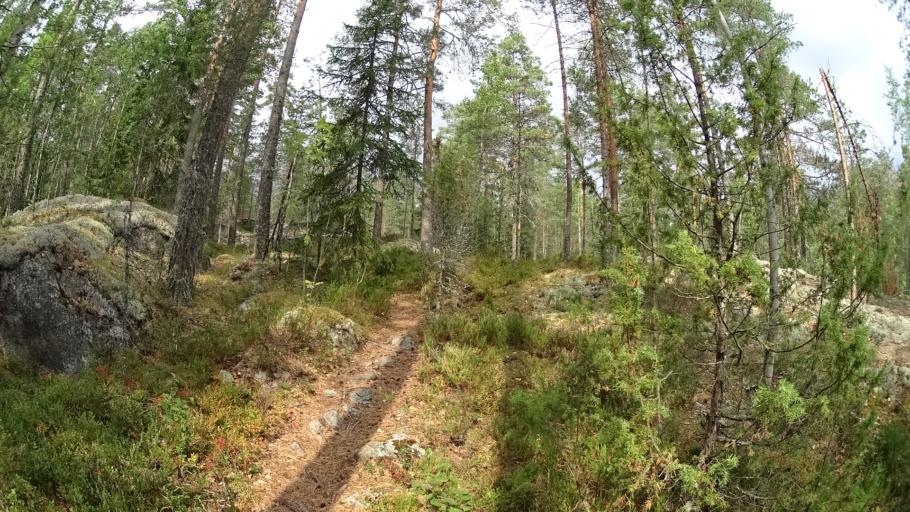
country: FI
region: Uusimaa
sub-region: Helsinki
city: Espoo
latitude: 60.3040
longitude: 24.5813
